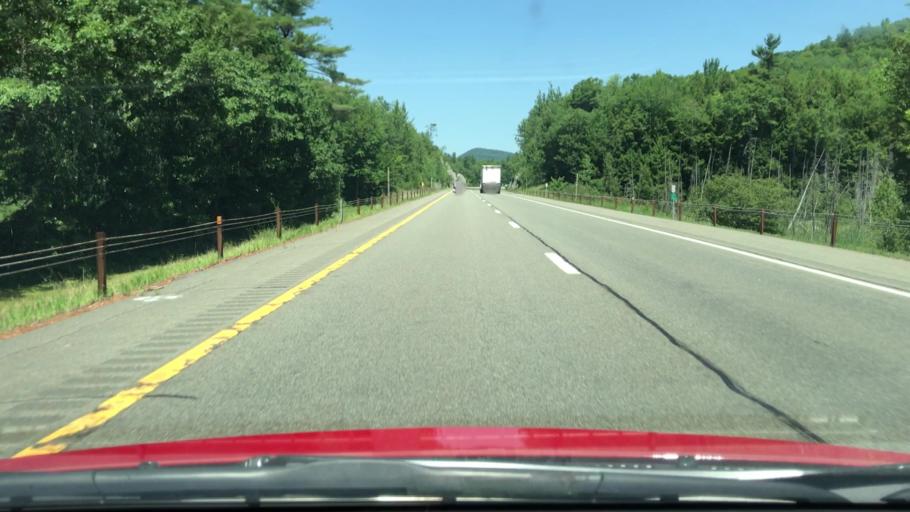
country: US
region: New York
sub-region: Essex County
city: Elizabethtown
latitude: 44.3312
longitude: -73.5318
